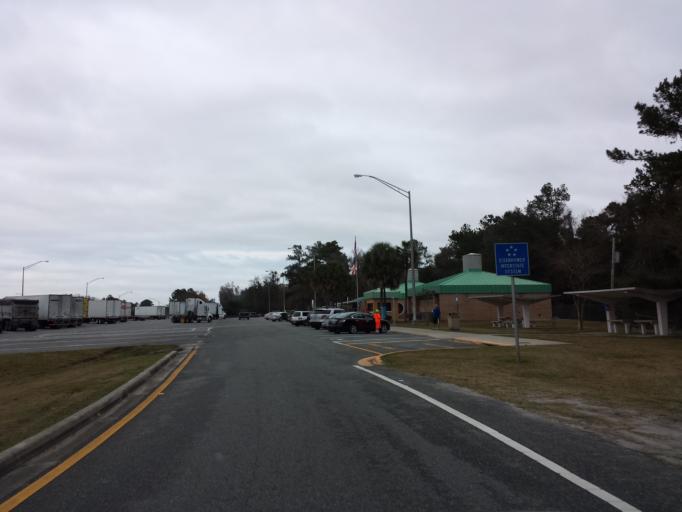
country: US
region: Florida
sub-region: Alachua County
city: High Springs
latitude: 29.9766
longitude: -82.5771
